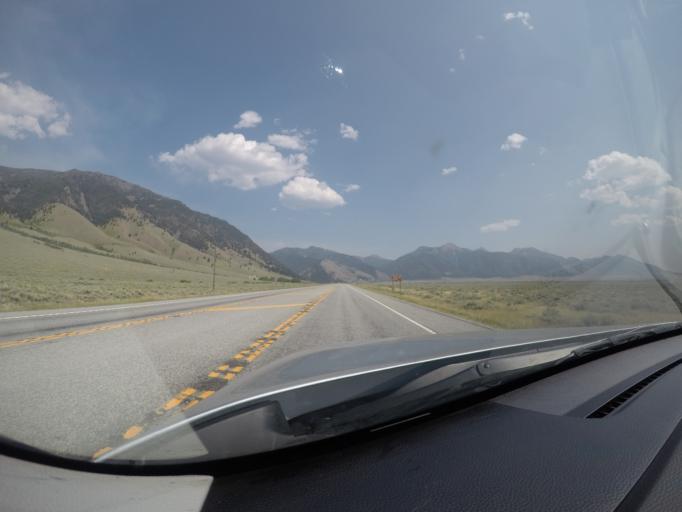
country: US
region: Montana
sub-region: Gallatin County
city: West Yellowstone
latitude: 44.8322
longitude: -111.4860
